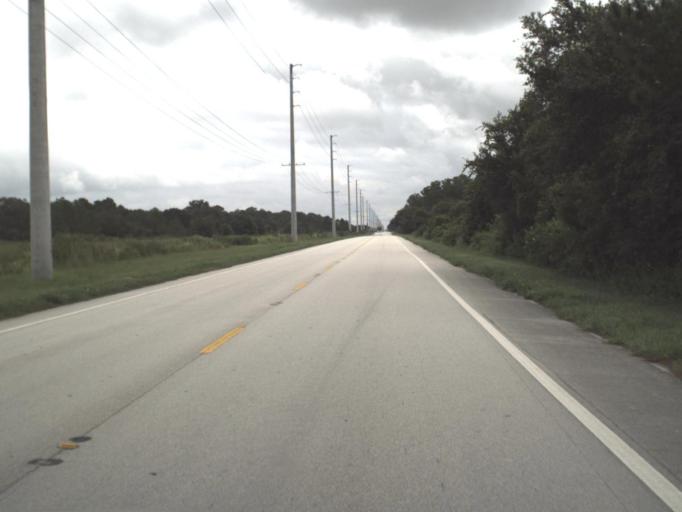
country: US
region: Florida
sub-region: Hardee County
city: Bowling Green
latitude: 27.5952
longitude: -82.0369
